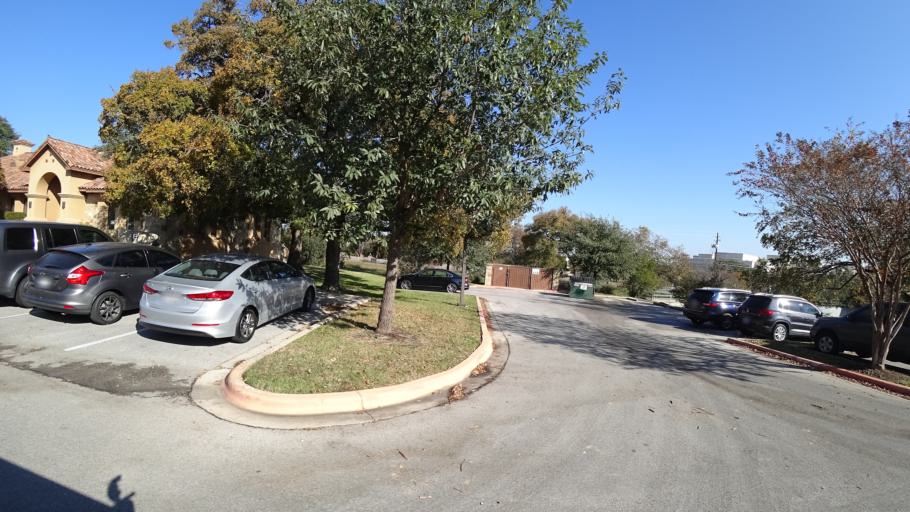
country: US
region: Texas
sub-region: Williamson County
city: Anderson Mill
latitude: 30.3925
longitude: -97.8434
